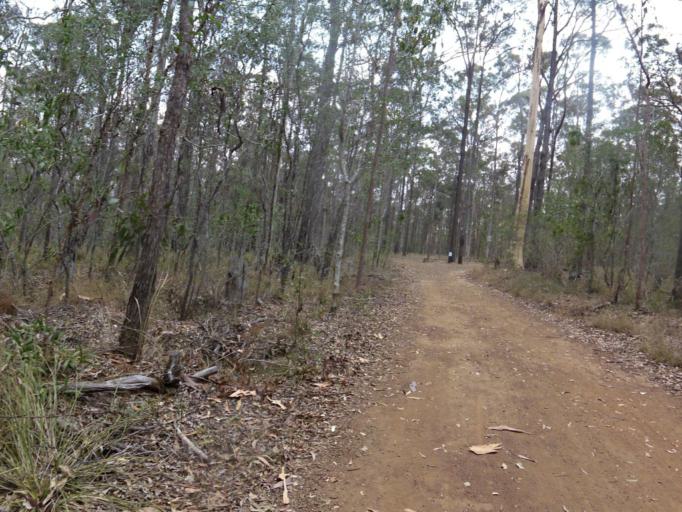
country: AU
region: Queensland
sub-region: Logan
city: Springwood
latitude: -27.6089
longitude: 153.1538
